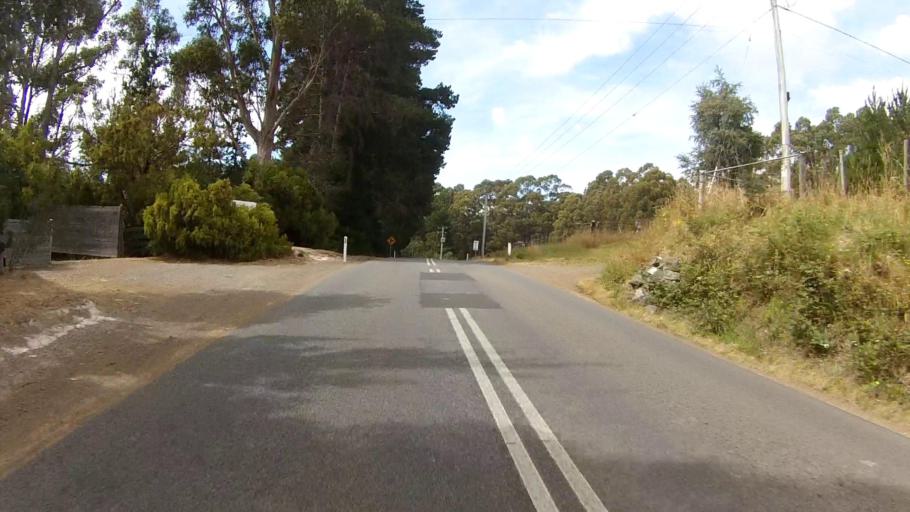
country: AU
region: Tasmania
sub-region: Kingborough
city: Kettering
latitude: -43.1788
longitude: 147.2373
